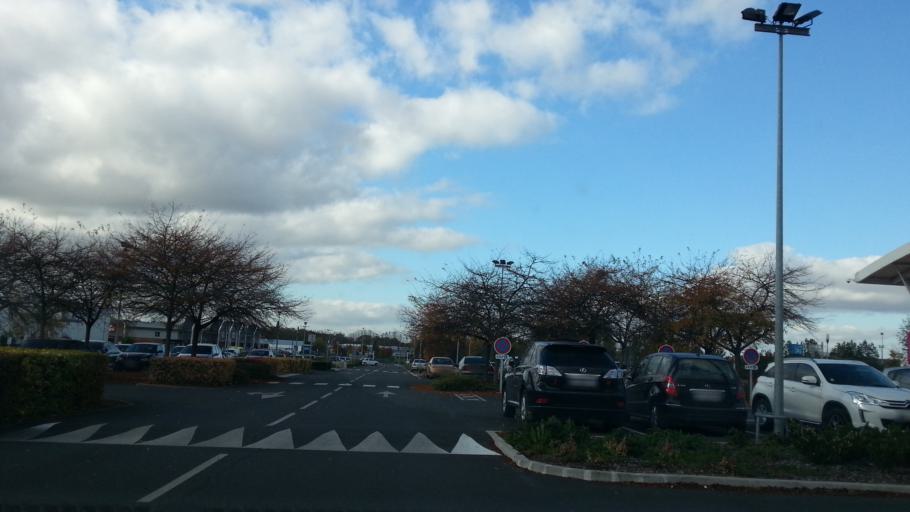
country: FR
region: Picardie
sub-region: Departement de l'Oise
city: Saint-Maximin
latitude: 49.2377
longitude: 2.4681
